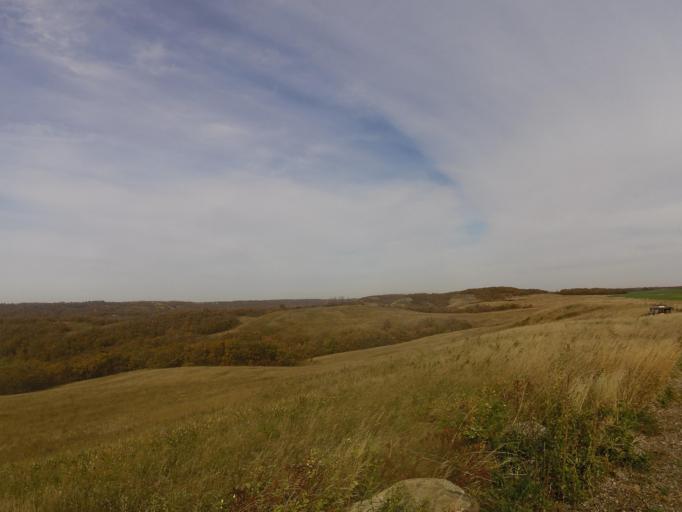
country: CA
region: Manitoba
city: Morden
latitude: 48.9400
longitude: -98.0613
